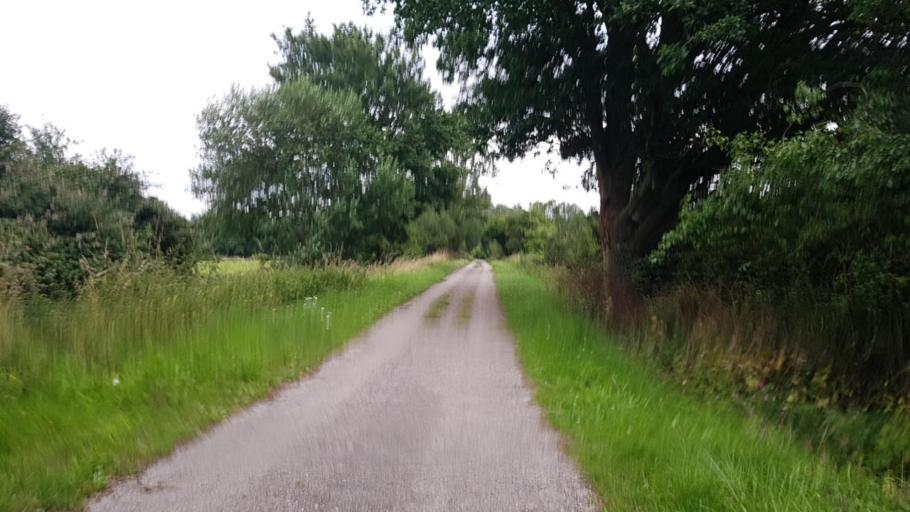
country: FR
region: Picardie
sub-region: Departement de l'Aisne
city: Buironfosse
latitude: 49.9028
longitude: 3.8673
